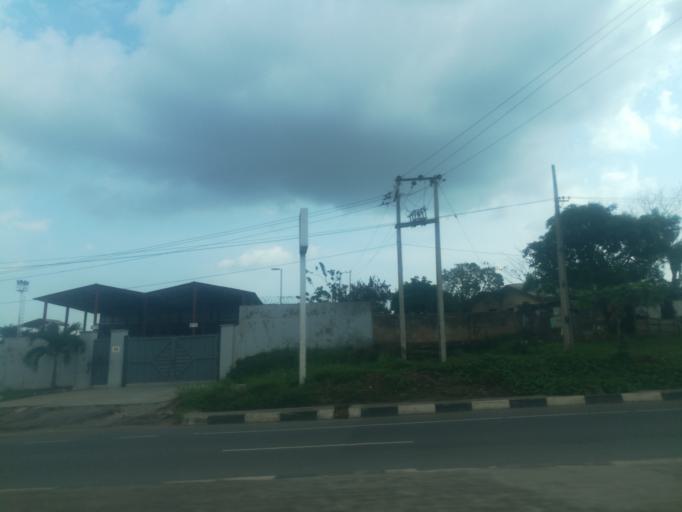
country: NG
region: Oyo
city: Ibadan
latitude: 7.3338
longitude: 3.8749
